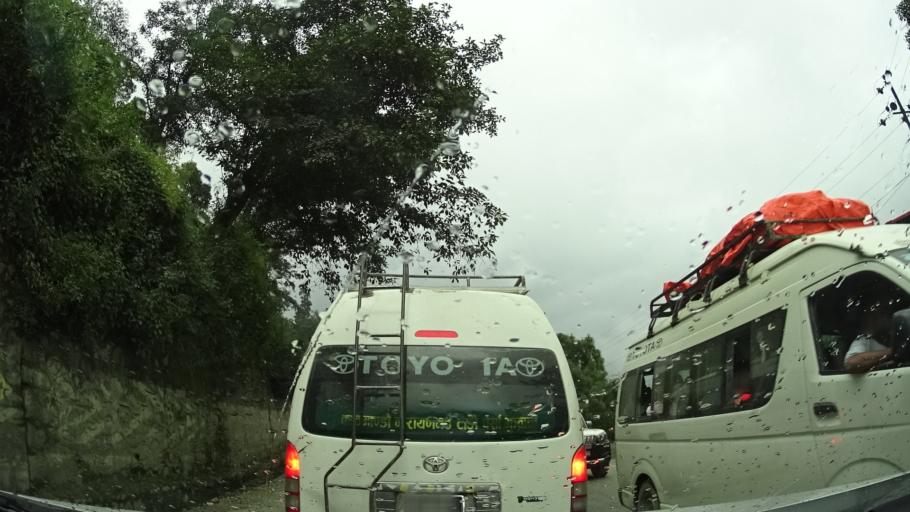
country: NP
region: Central Region
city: Kirtipur
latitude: 27.7088
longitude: 85.2040
